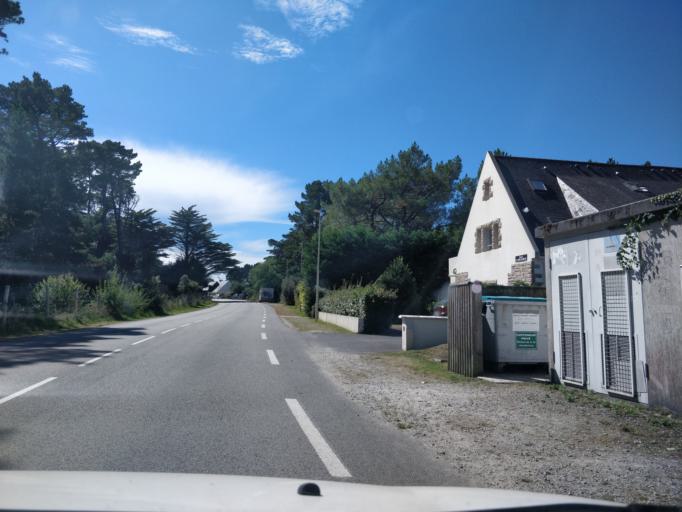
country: FR
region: Brittany
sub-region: Departement du Morbihan
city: Saint-Philibert
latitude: 47.5712
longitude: -2.9995
